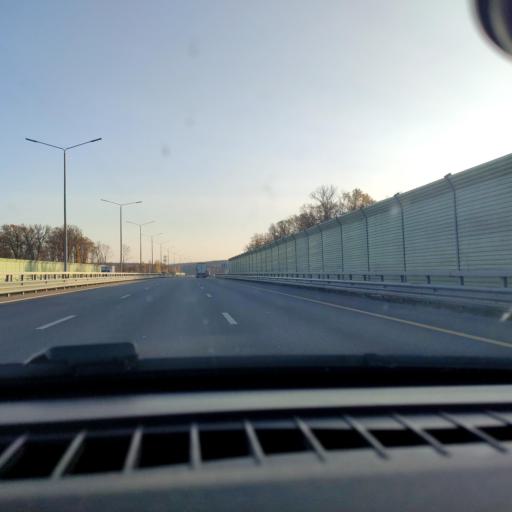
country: RU
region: Voronezj
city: Ramon'
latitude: 51.8174
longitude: 39.2524
